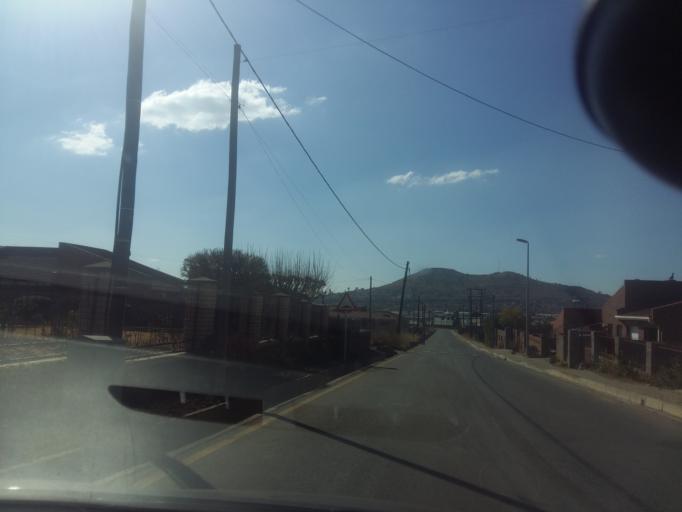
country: LS
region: Maseru
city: Maseru
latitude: -29.3467
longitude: 27.4502
